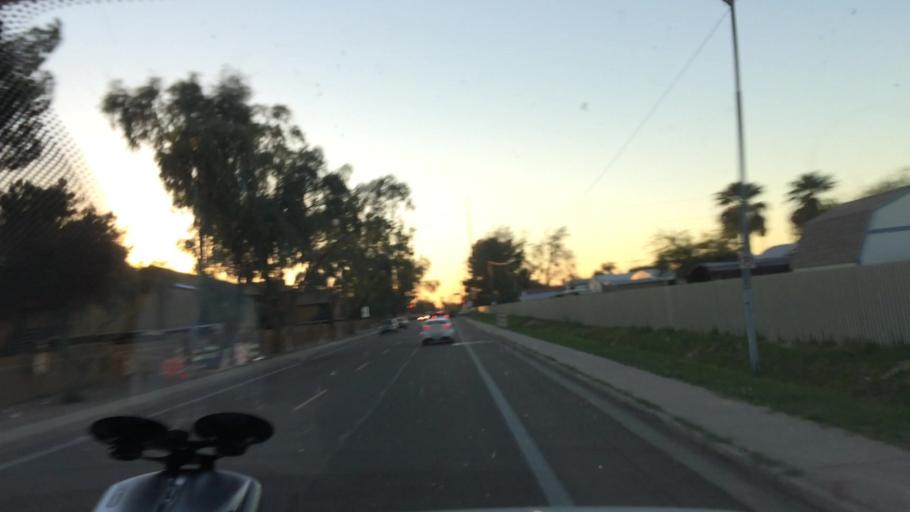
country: US
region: Arizona
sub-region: Maricopa County
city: Glendale
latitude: 33.6476
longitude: -112.0629
